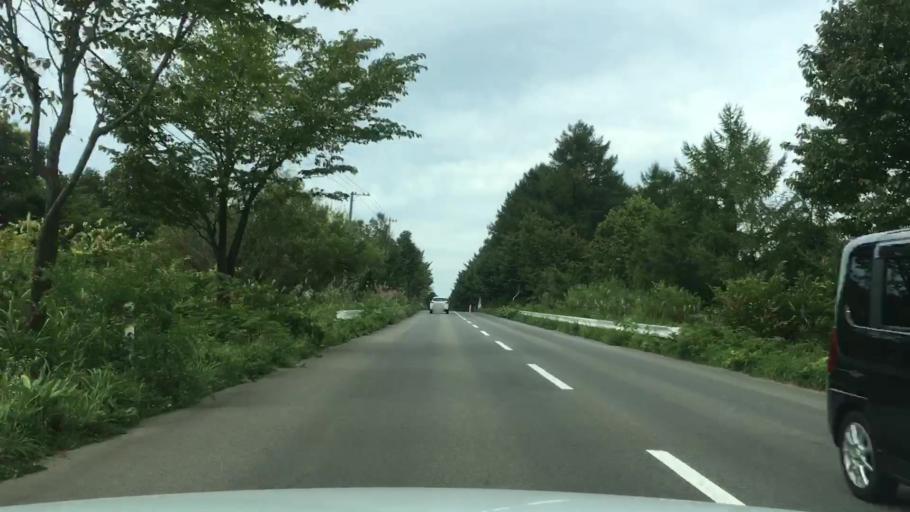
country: JP
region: Aomori
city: Shimokizukuri
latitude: 40.7105
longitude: 140.3333
